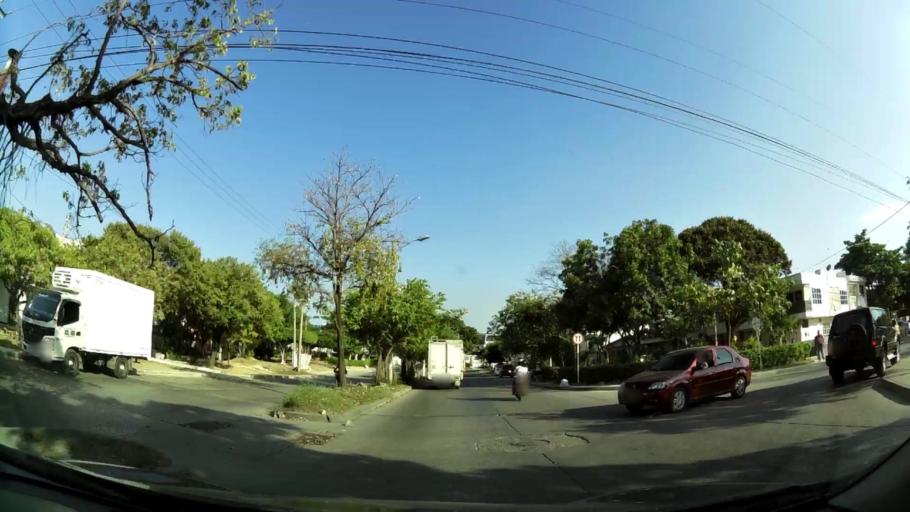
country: CO
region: Bolivar
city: Cartagena
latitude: 10.3861
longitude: -75.4809
